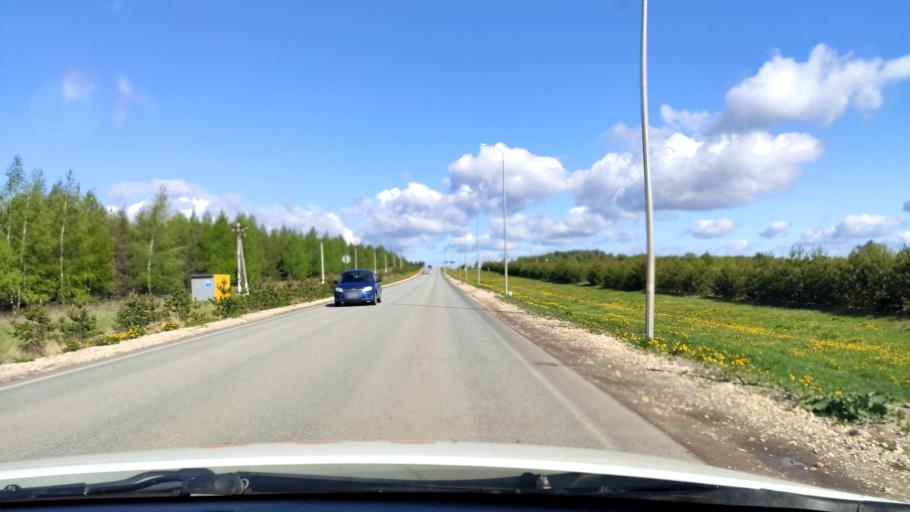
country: RU
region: Tatarstan
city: Sviyazhsk
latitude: 55.7268
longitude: 48.7472
